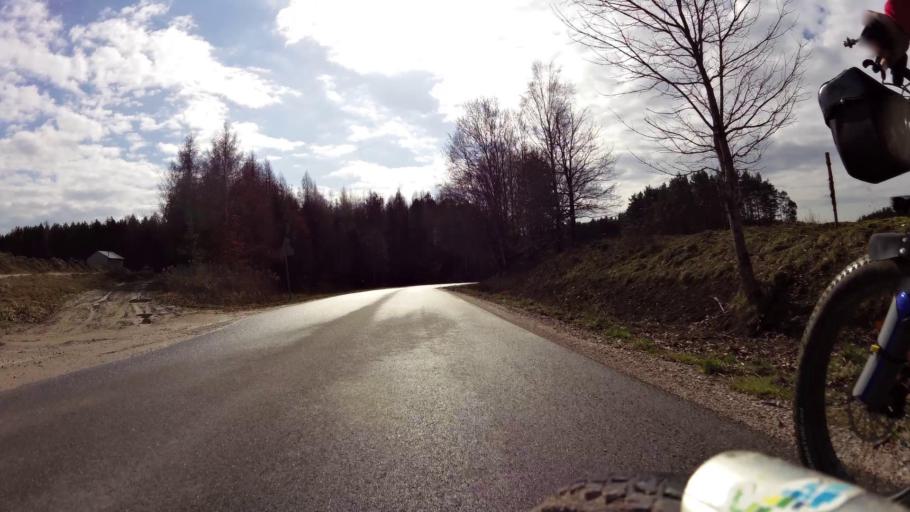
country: PL
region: Pomeranian Voivodeship
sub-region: Powiat bytowski
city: Kolczyglowy
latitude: 54.2079
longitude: 17.2355
